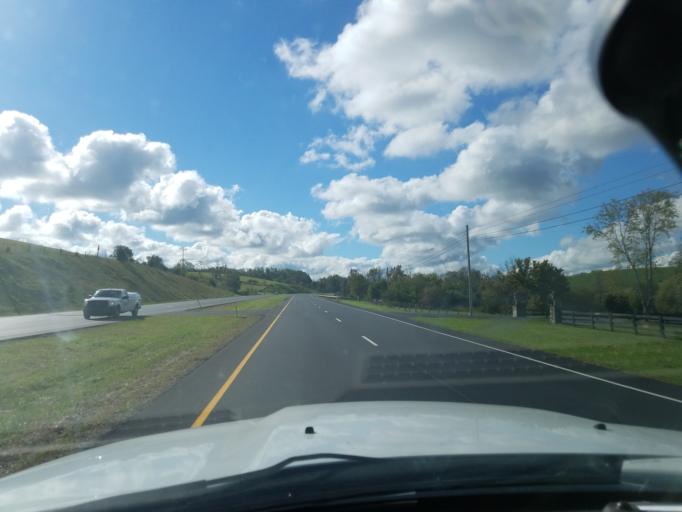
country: US
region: Kentucky
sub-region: Boyle County
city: Danville
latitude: 37.6107
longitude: -84.7284
